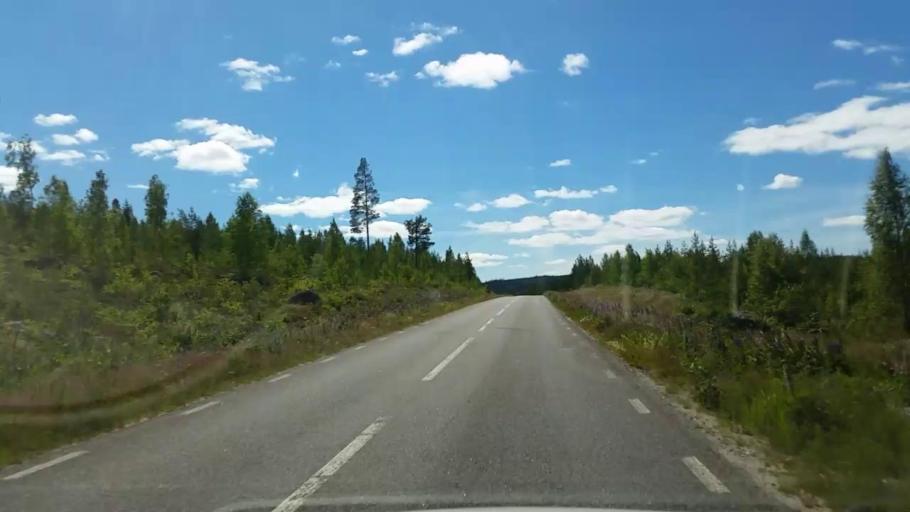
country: SE
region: Gaevleborg
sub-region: Ljusdals Kommun
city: Farila
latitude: 61.6212
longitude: 15.5499
